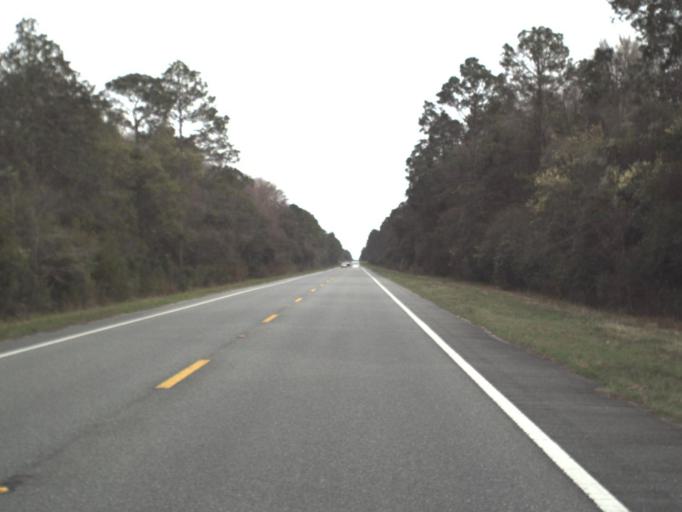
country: US
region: Florida
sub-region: Wakulla County
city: Crawfordville
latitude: 30.3222
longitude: -84.4537
